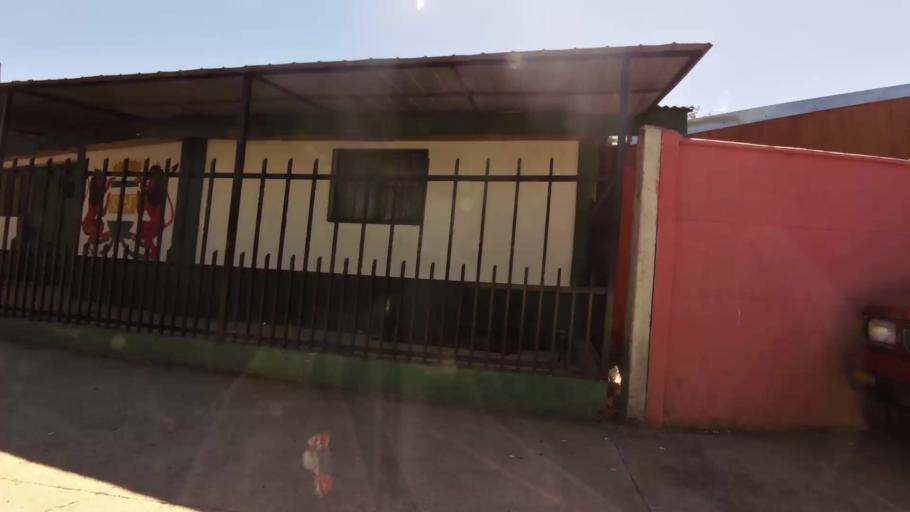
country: CL
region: O'Higgins
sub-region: Provincia de Colchagua
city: Chimbarongo
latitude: -34.5761
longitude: -70.9878
